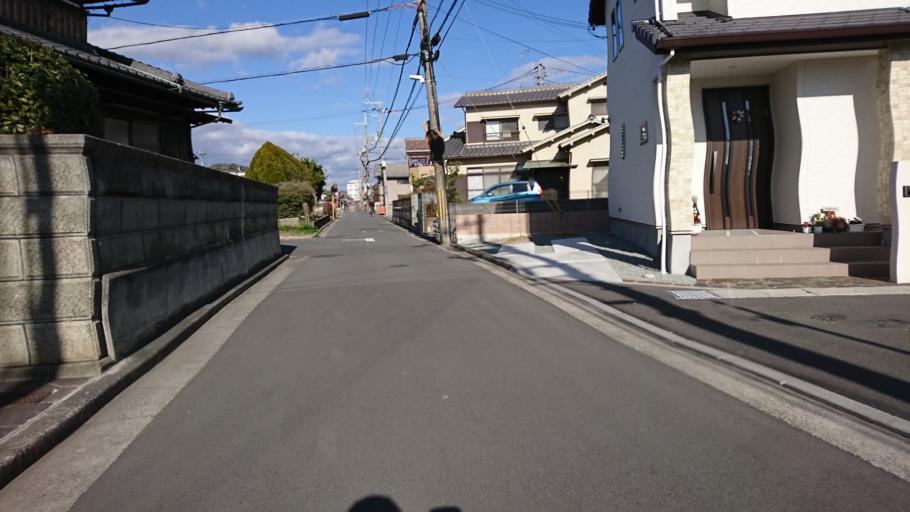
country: JP
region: Hyogo
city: Kakogawacho-honmachi
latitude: 34.7721
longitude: 134.7739
